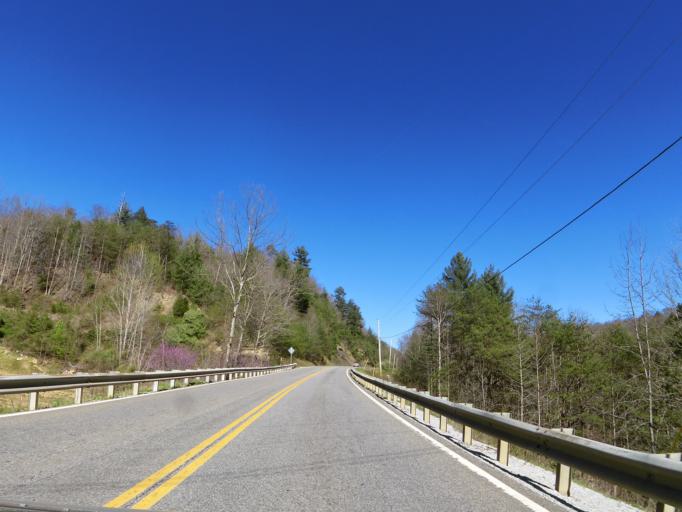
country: US
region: Tennessee
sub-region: Scott County
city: Huntsville
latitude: 36.4329
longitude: -84.4535
